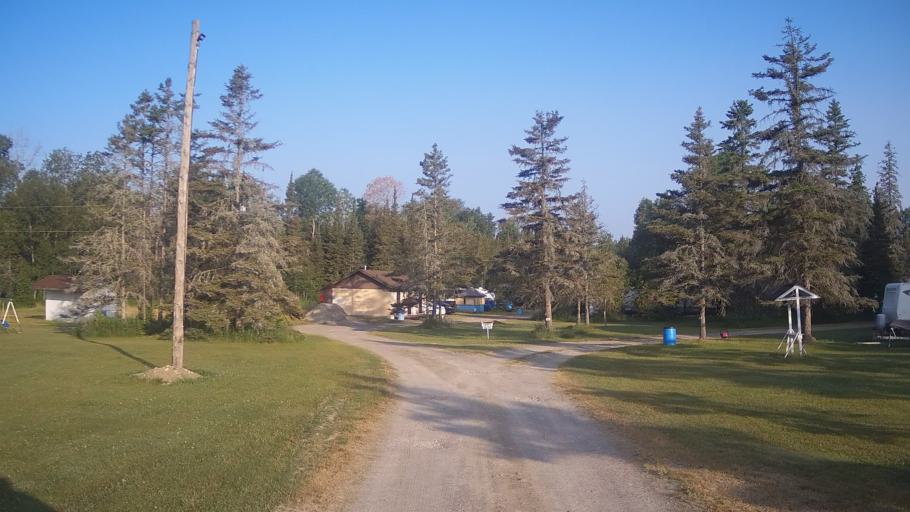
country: CA
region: Ontario
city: Rayside-Balfour
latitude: 46.5749
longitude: -81.3113
